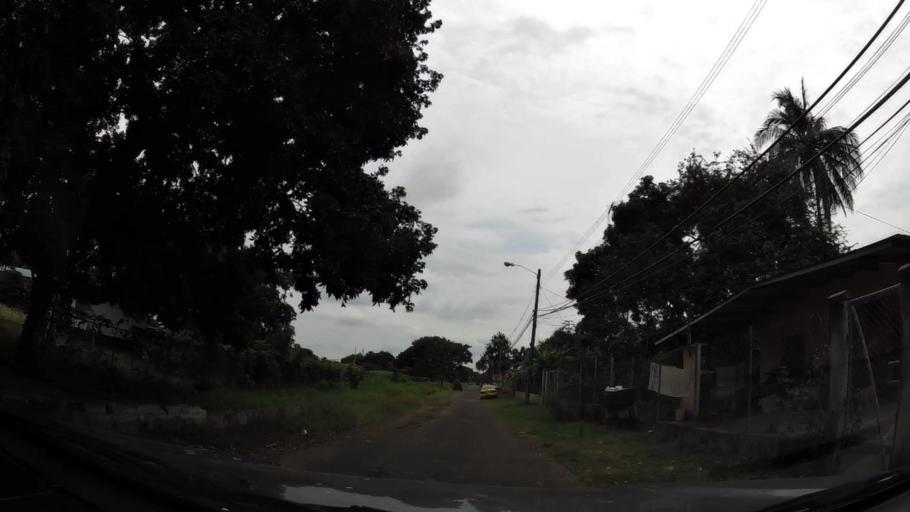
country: PA
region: Panama
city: San Miguelito
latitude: 9.0482
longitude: -79.4297
